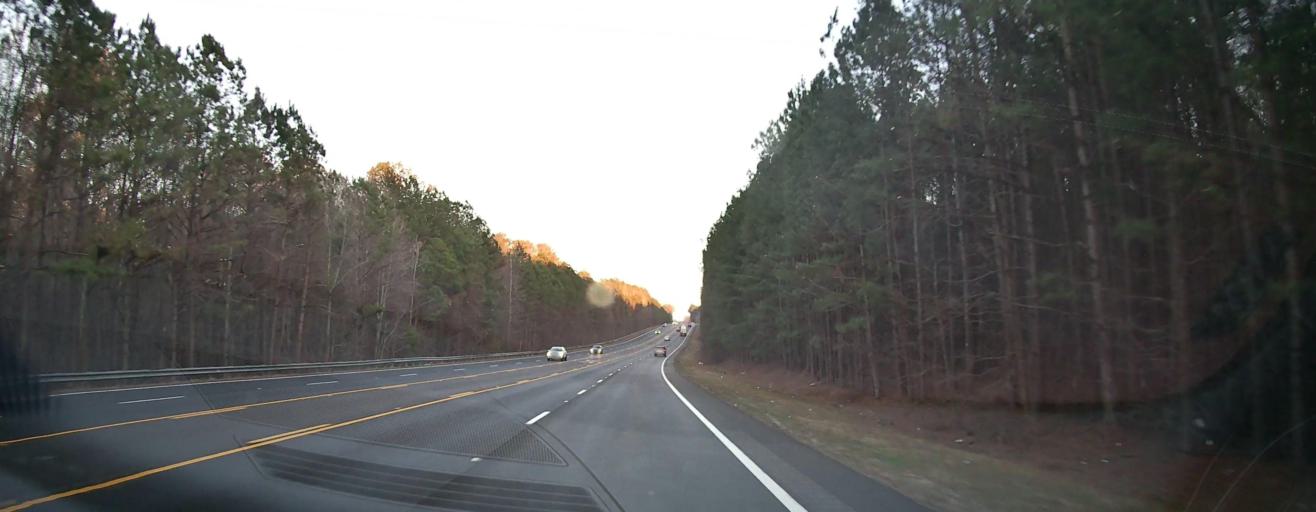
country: US
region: Georgia
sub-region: Clayton County
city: Riverdale
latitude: 33.5515
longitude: -84.4783
